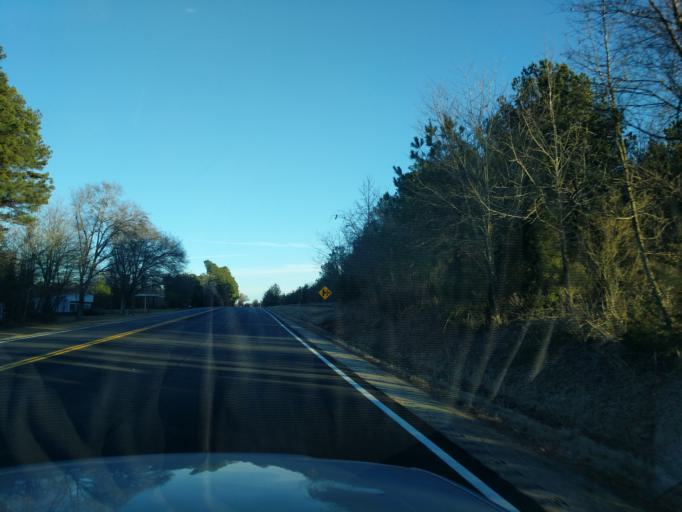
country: US
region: Georgia
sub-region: Stephens County
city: Toccoa
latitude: 34.5127
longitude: -83.2234
